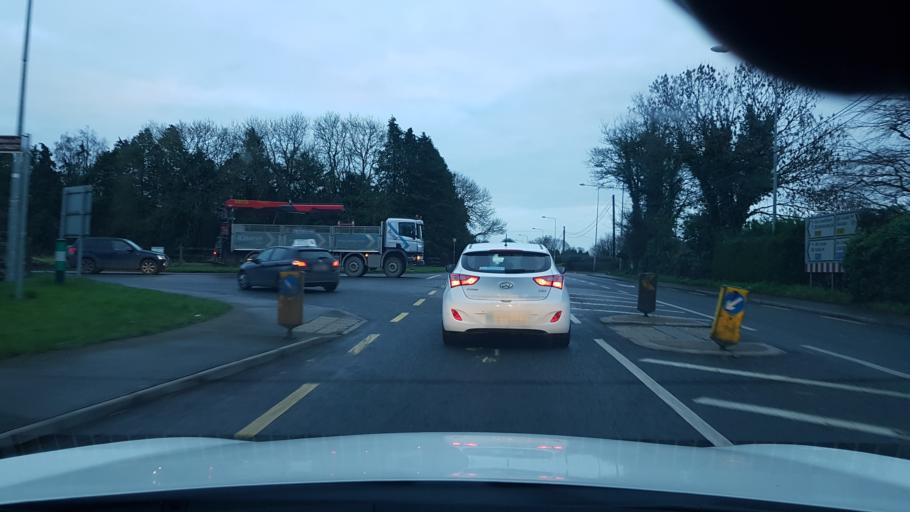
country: IE
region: Leinster
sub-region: An Mhi
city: Dunshaughlin
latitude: 53.5672
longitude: -6.5798
